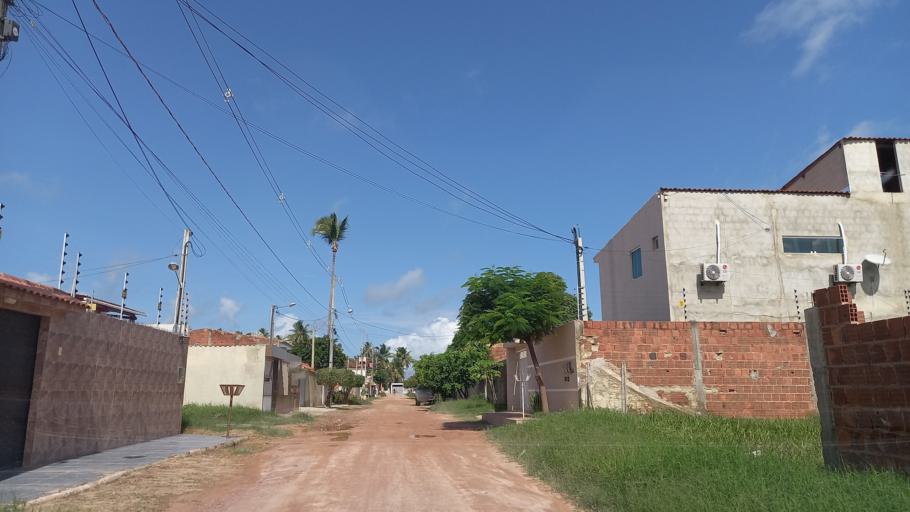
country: BR
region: Pernambuco
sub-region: Sao Jose Da Coroa Grande
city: Sao Jose da Coroa Grande
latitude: -8.9229
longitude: -35.1609
